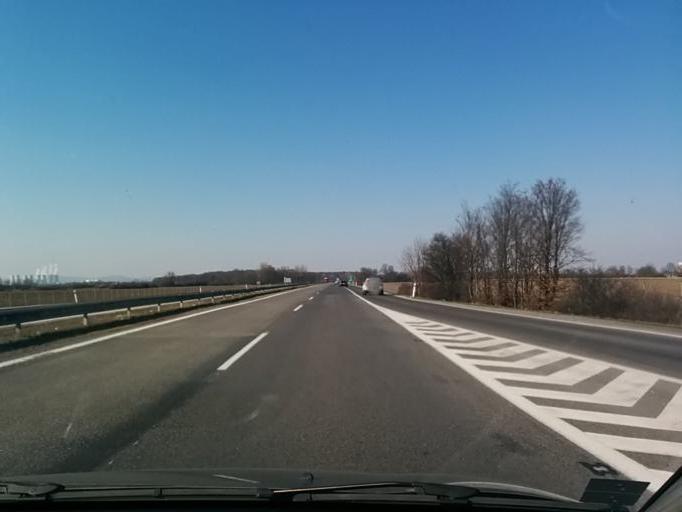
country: SK
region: Trnavsky
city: Leopoldov
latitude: 48.4392
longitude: 17.7399
